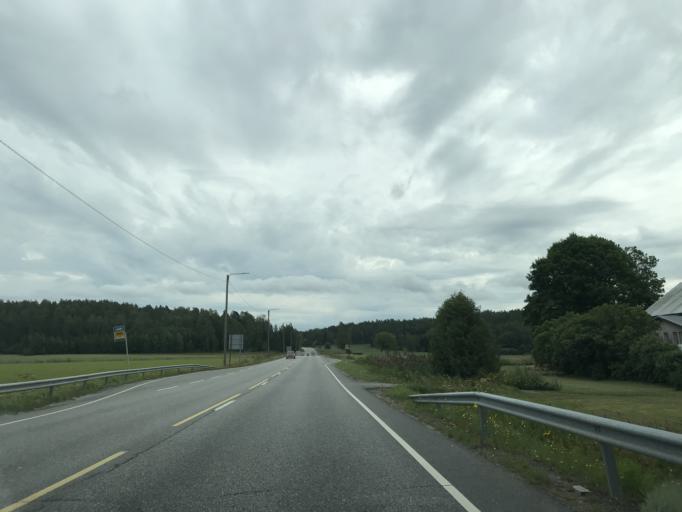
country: FI
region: Varsinais-Suomi
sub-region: Turku
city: Piikkioe
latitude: 60.4340
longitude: 22.5917
